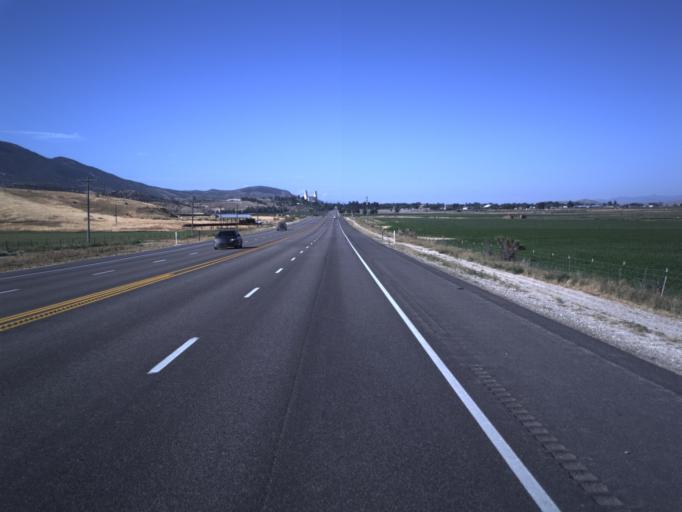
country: US
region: Utah
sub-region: Sanpete County
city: Manti
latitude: 39.3021
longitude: -111.6174
